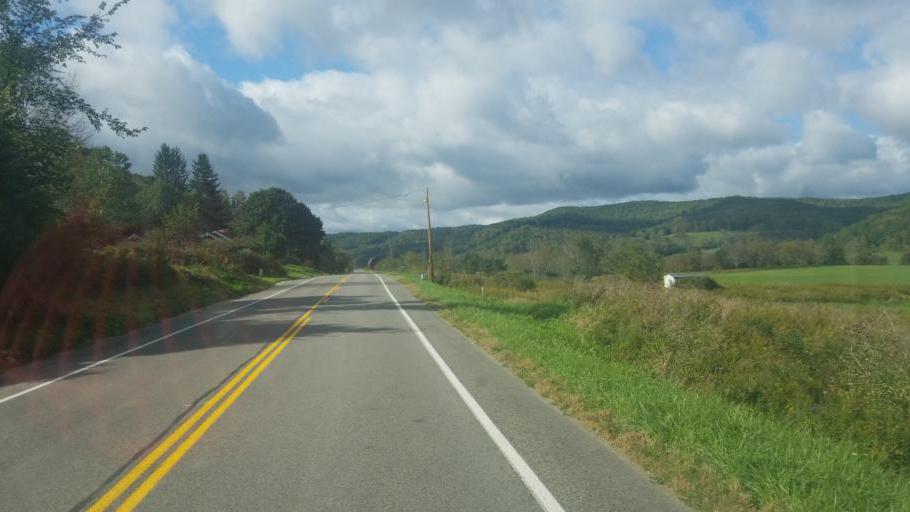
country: US
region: New York
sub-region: Cattaraugus County
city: Weston Mills
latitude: 42.1388
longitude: -78.3302
